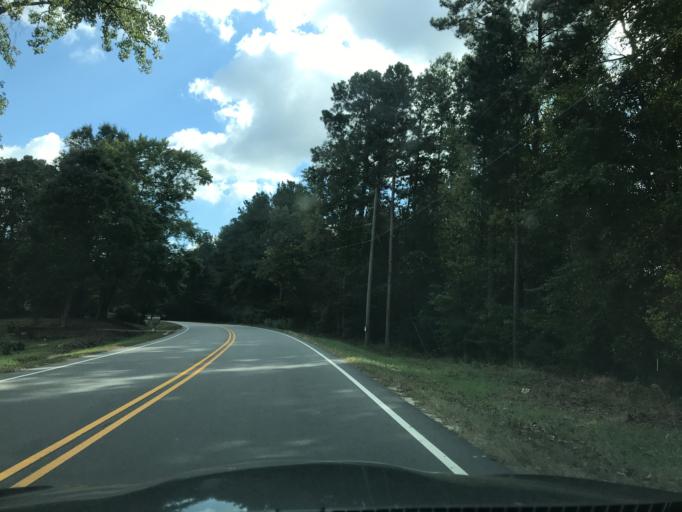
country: US
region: North Carolina
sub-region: Wake County
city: Wake Forest
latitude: 35.9267
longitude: -78.5266
